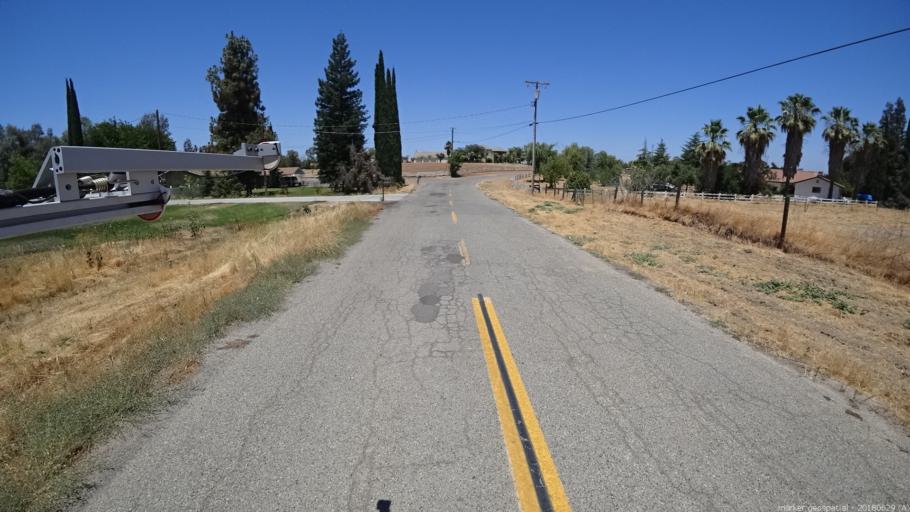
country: US
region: California
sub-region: Madera County
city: Parksdale
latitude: 36.9981
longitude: -119.9827
